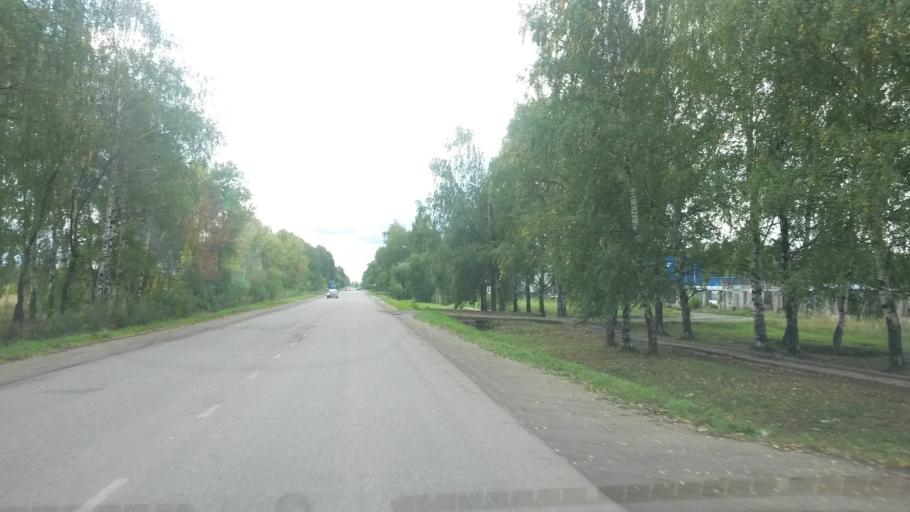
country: RU
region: Ivanovo
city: Zavolzhsk
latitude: 57.4769
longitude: 42.1527
